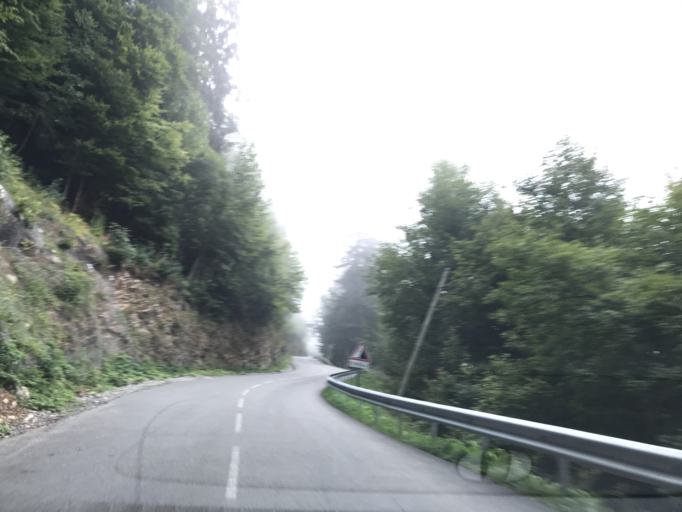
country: FR
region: Rhone-Alpes
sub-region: Departement de la Haute-Savoie
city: Talloires
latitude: 45.8166
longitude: 6.2441
